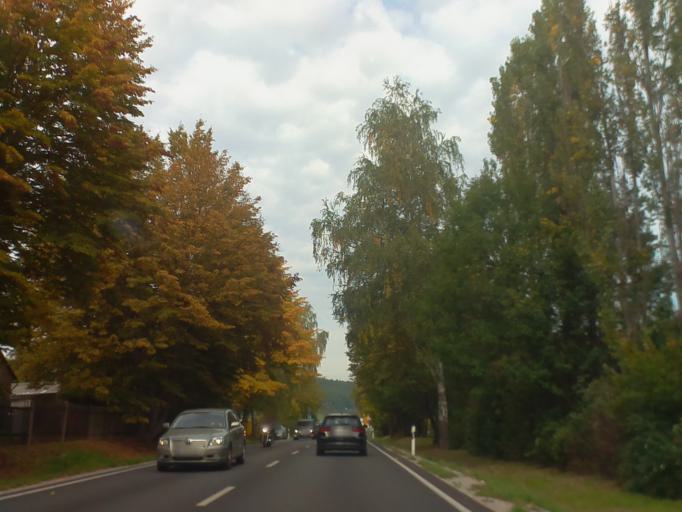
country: DE
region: Thuringia
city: Kahla
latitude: 50.8069
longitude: 11.5784
